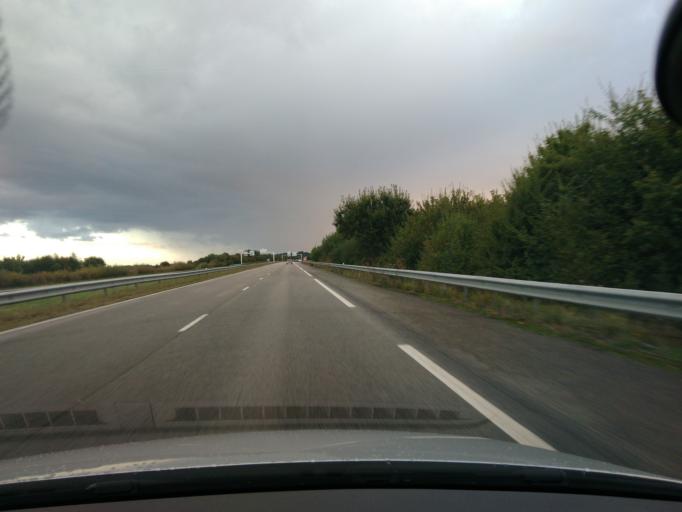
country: FR
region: Haute-Normandie
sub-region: Departement de l'Eure
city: Evreux
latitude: 49.0054
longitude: 1.1864
